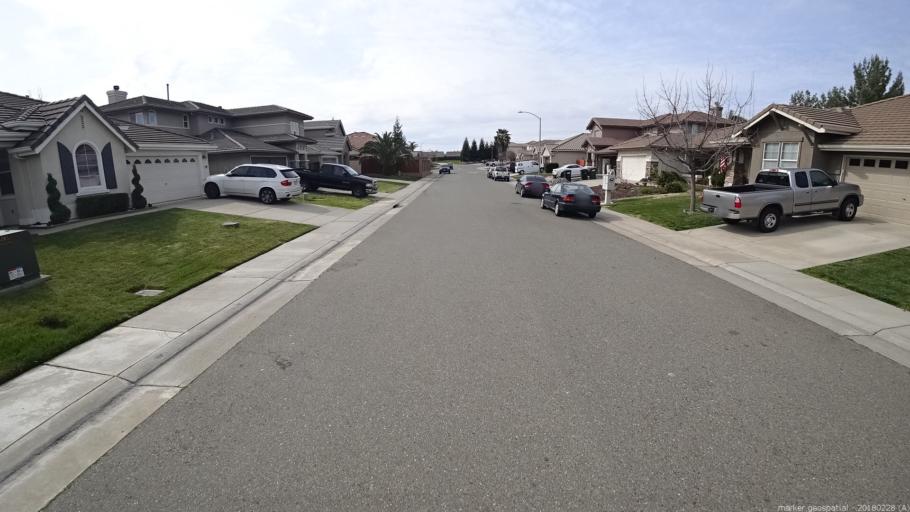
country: US
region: California
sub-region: Sacramento County
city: Antelope
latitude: 38.7102
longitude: -121.3408
